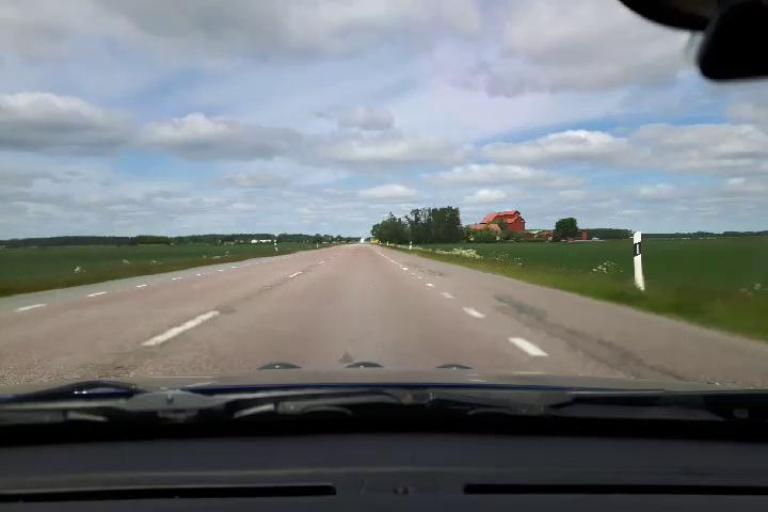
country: SE
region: Uppsala
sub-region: Uppsala Kommun
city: Gamla Uppsala
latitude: 59.9167
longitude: 17.6046
